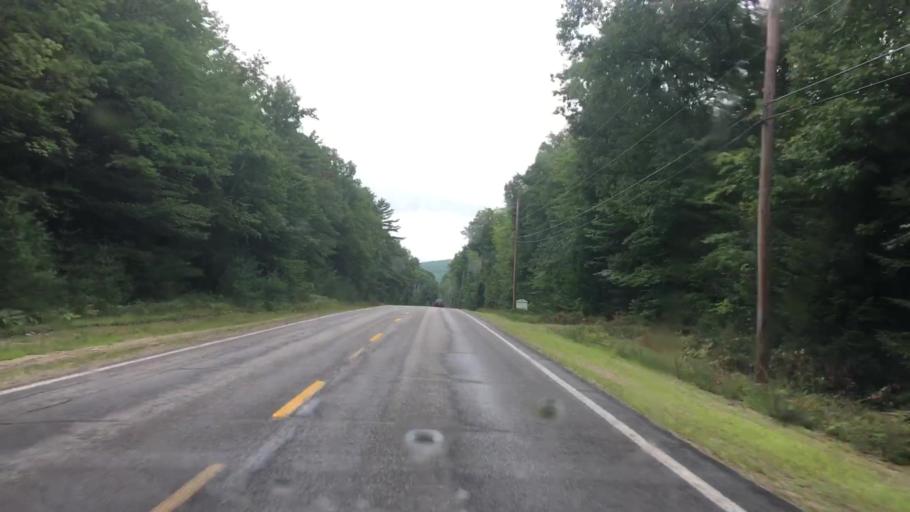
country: US
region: Maine
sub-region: Oxford County
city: Fryeburg
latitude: 43.9932
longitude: -70.9378
